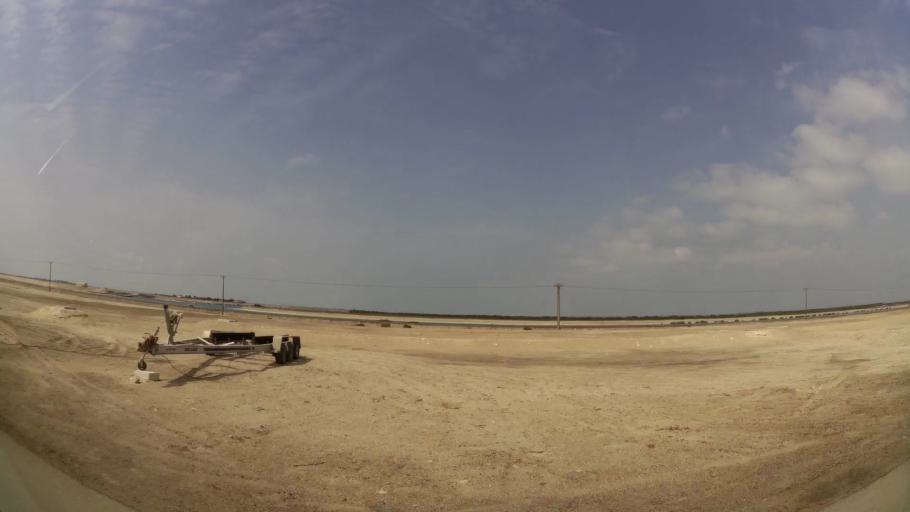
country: AE
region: Abu Dhabi
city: Abu Dhabi
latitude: 24.5631
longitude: 54.6377
